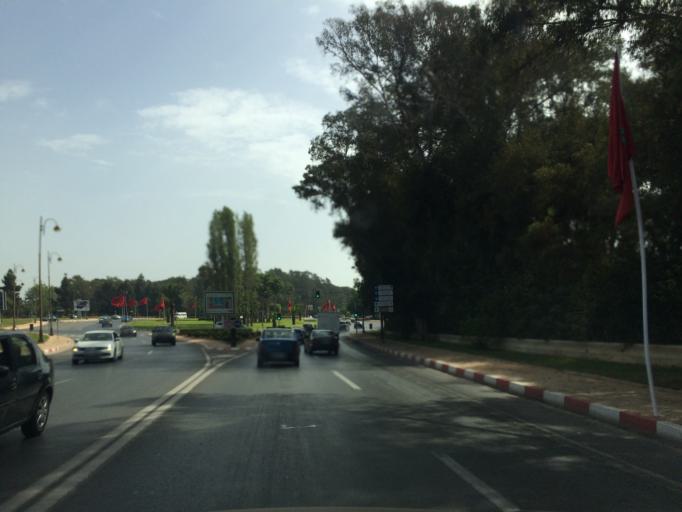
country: MA
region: Rabat-Sale-Zemmour-Zaer
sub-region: Rabat
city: Rabat
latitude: 33.9947
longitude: -6.8380
